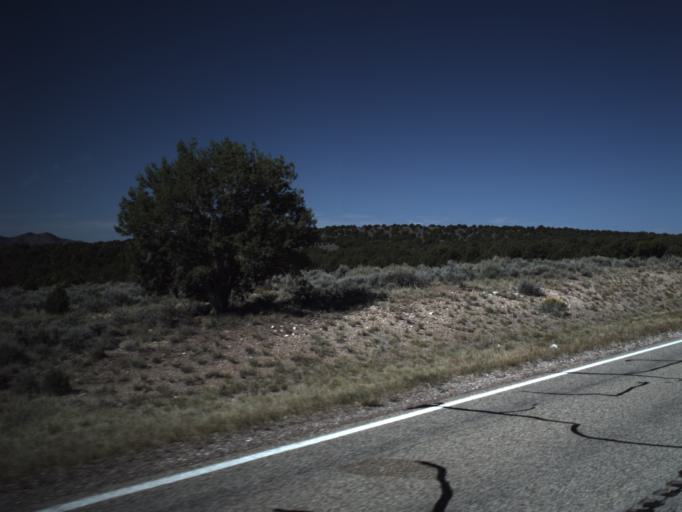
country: US
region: Utah
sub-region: Washington County
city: Enterprise
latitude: 37.6581
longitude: -113.4582
